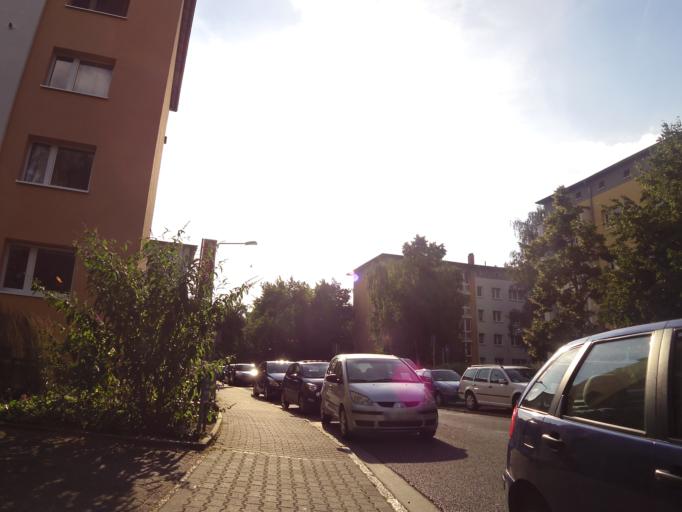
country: DE
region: Hesse
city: Niederrad
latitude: 50.0840
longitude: 8.6419
